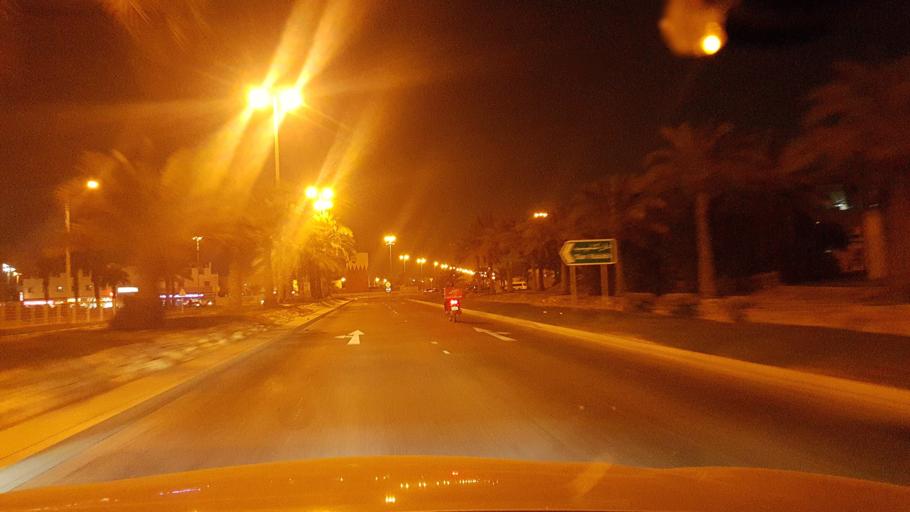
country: BH
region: Central Governorate
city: Dar Kulayb
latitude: 26.0612
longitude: 50.5082
